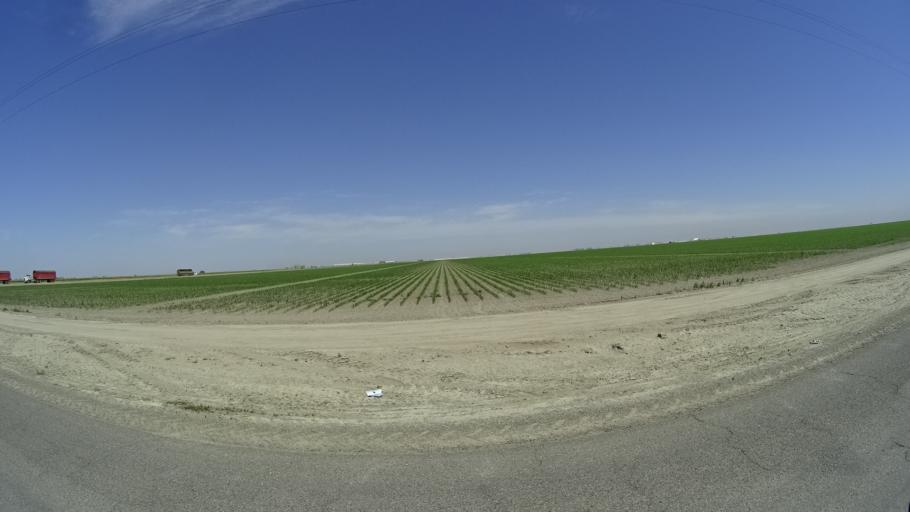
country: US
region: California
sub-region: Kings County
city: Corcoran
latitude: 36.1379
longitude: -119.6892
